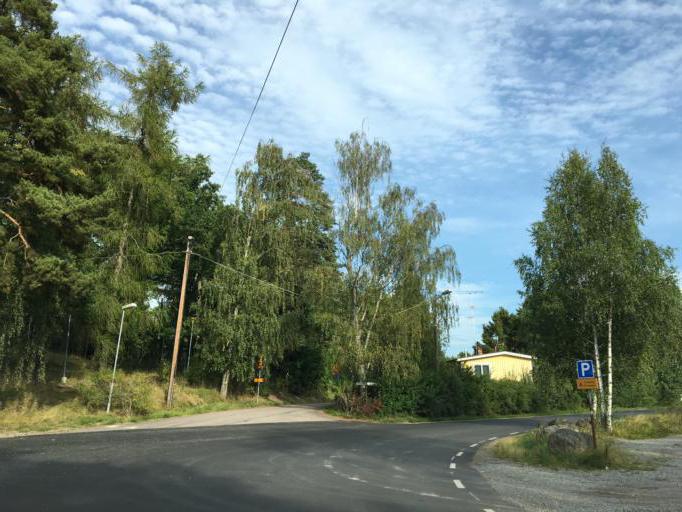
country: SE
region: Soedermanland
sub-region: Eskilstuna Kommun
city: Torshalla
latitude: 59.4519
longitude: 16.4351
